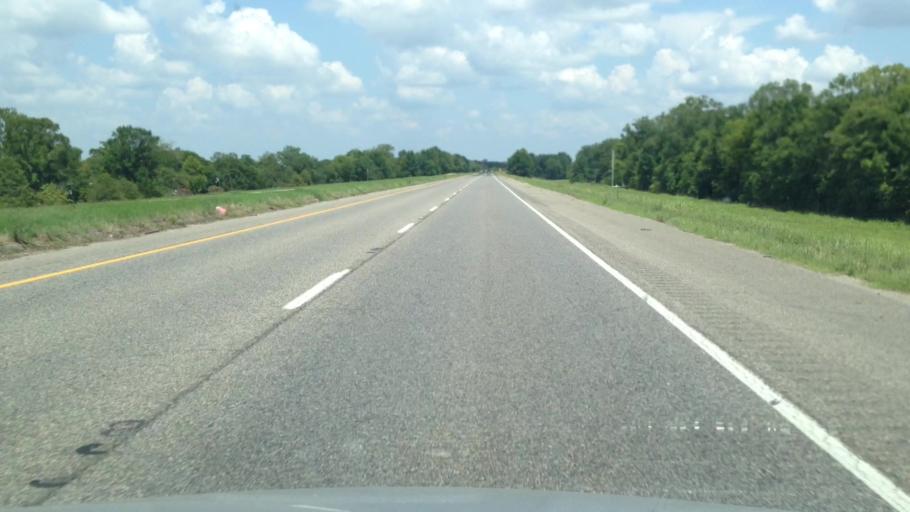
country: US
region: Louisiana
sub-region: Saint Landry Parish
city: Krotz Springs
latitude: 30.5487
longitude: -91.8428
